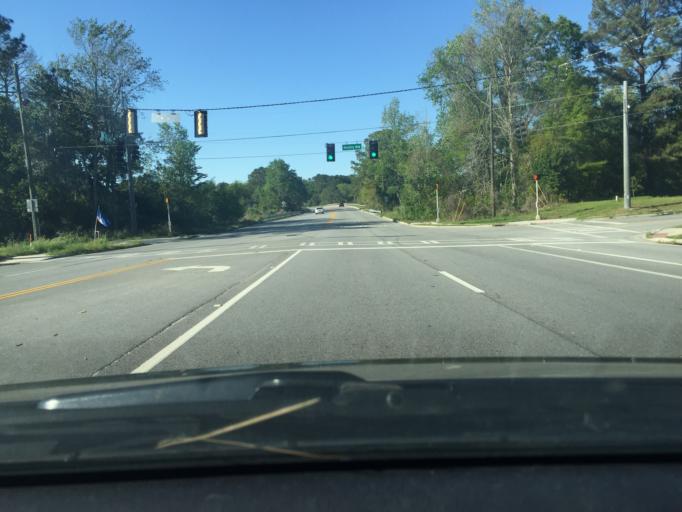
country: US
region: Georgia
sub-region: Chatham County
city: Isle of Hope
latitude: 31.9856
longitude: -81.1050
